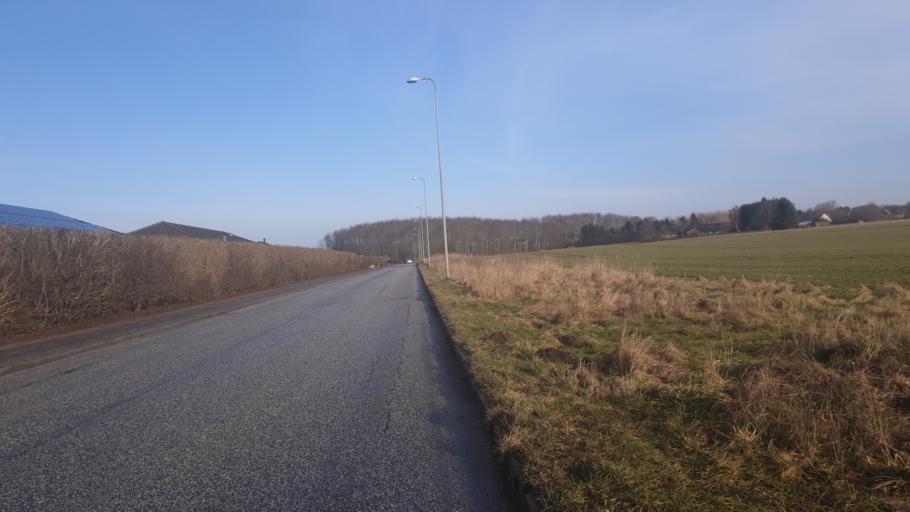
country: DK
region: Central Jutland
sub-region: Hedensted Kommune
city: Hedensted
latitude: 55.7701
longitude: 9.7201
